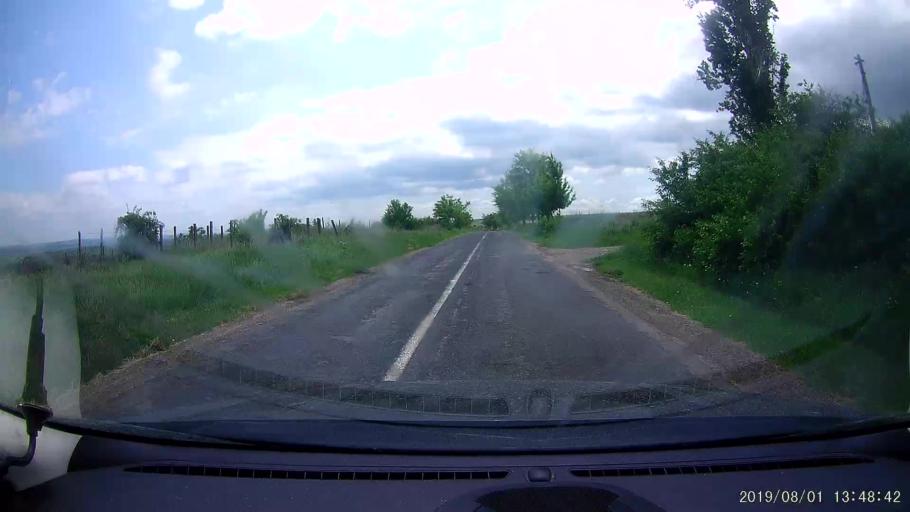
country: RO
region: Galati
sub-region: Comuna Oancea
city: Oancea
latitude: 45.9041
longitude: 28.1105
